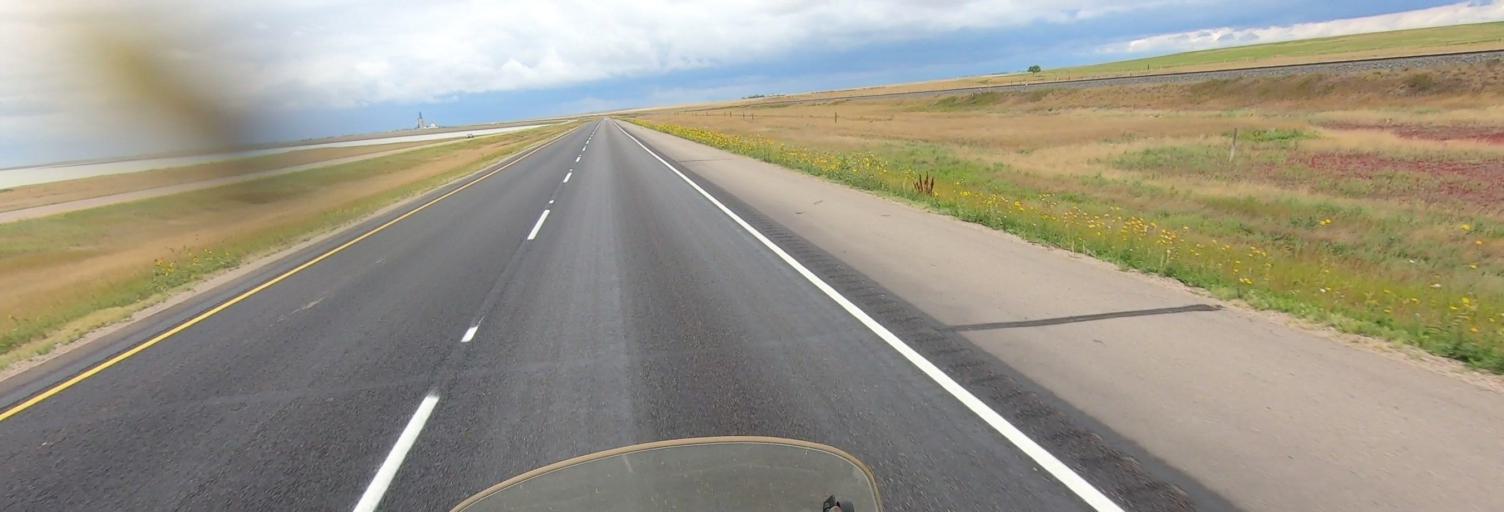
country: CA
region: Saskatchewan
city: Swift Current
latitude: 50.4172
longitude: -107.0882
